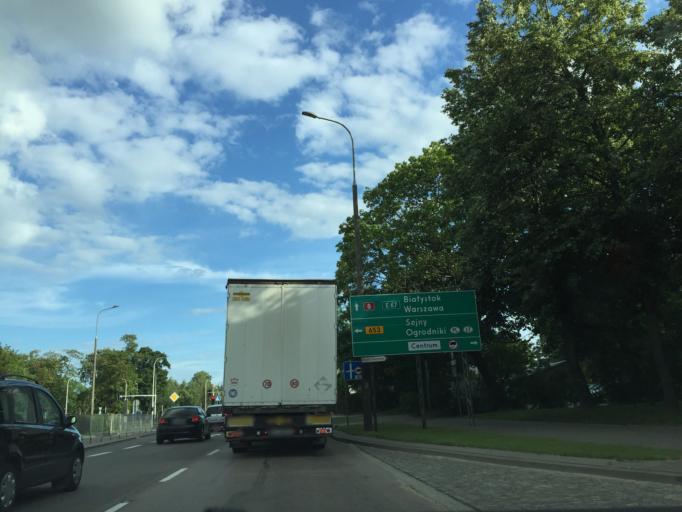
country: PL
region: Podlasie
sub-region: Suwalki
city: Suwalki
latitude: 54.1027
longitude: 22.9386
